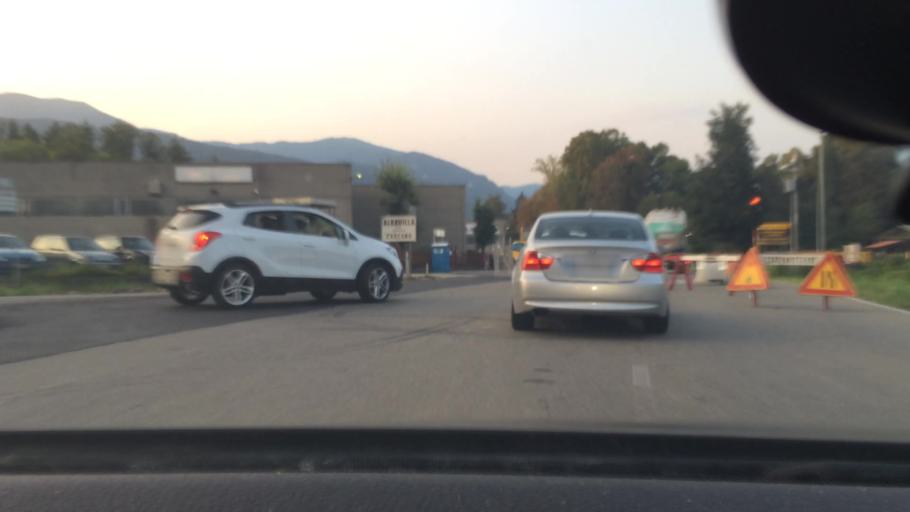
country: IT
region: Lombardy
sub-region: Provincia di Como
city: Alserio
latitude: 45.7874
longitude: 9.1964
